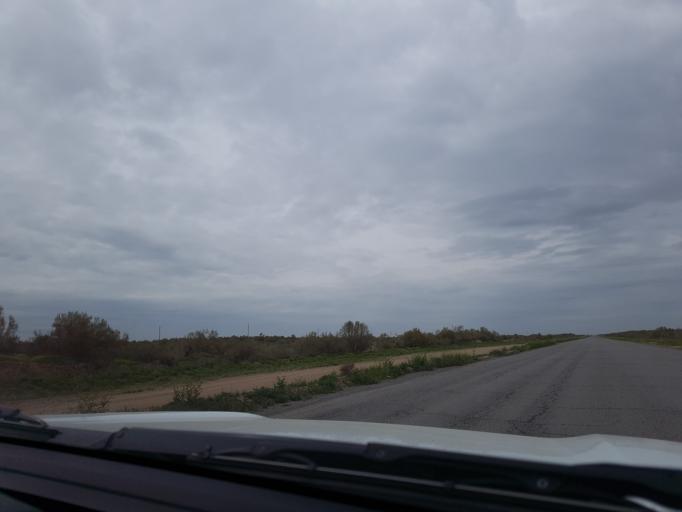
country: TM
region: Mary
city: Bayramaly
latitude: 37.8168
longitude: 62.5735
